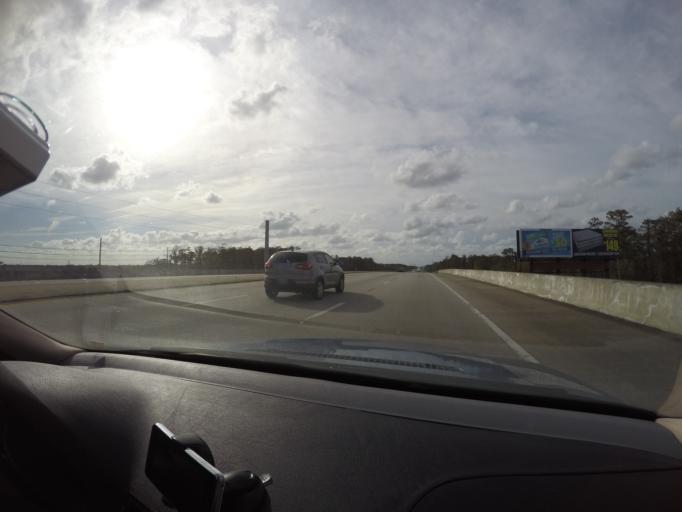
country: US
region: Florida
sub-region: Orange County
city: Belle Isle
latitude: 28.4512
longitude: -81.3669
